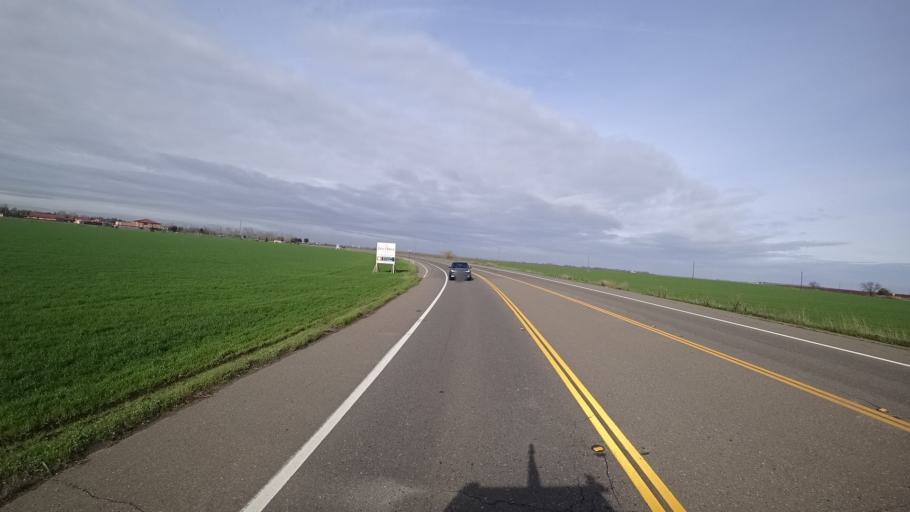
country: US
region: California
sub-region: Yolo County
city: Davis
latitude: 38.5635
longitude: -121.6953
